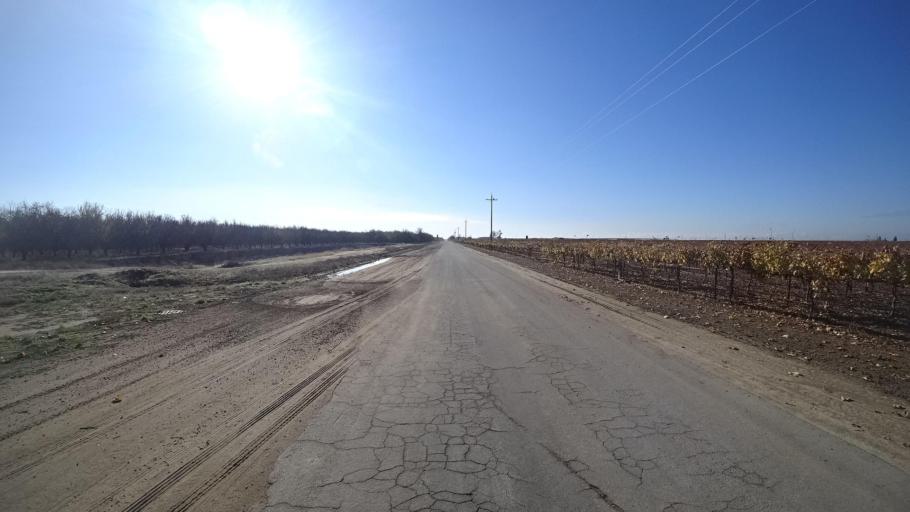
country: US
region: California
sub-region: Kern County
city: McFarland
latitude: 35.6957
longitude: -119.2674
